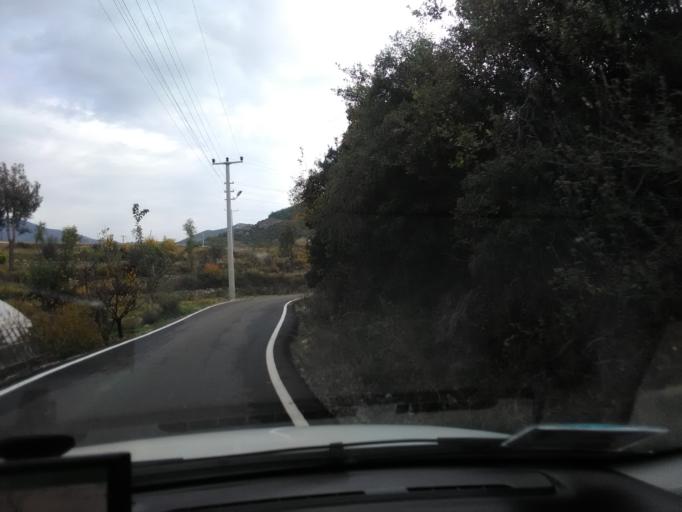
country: TR
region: Antalya
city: Gazipasa
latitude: 36.2590
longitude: 32.3600
